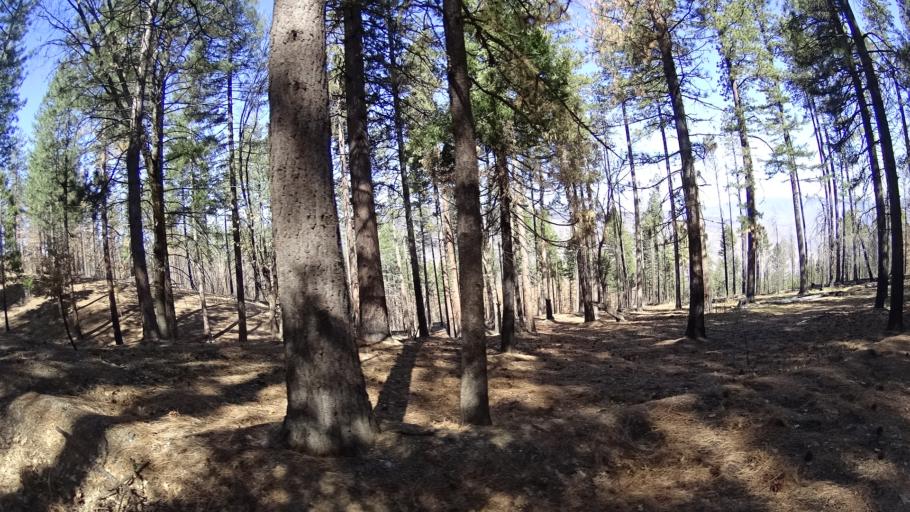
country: US
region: California
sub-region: Tehama County
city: Rancho Tehama Reserve
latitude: 39.6546
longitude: -122.7242
